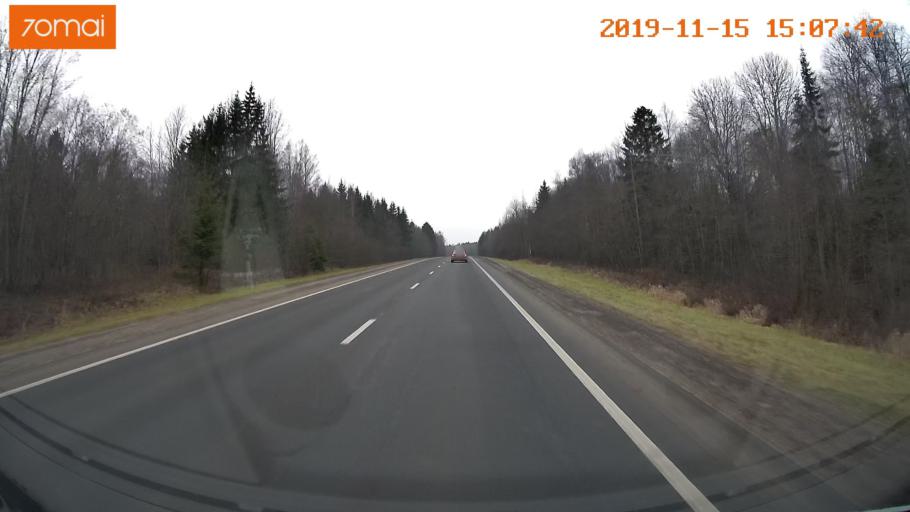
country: RU
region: Jaroslavl
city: Prechistoye
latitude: 58.3804
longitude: 40.2900
